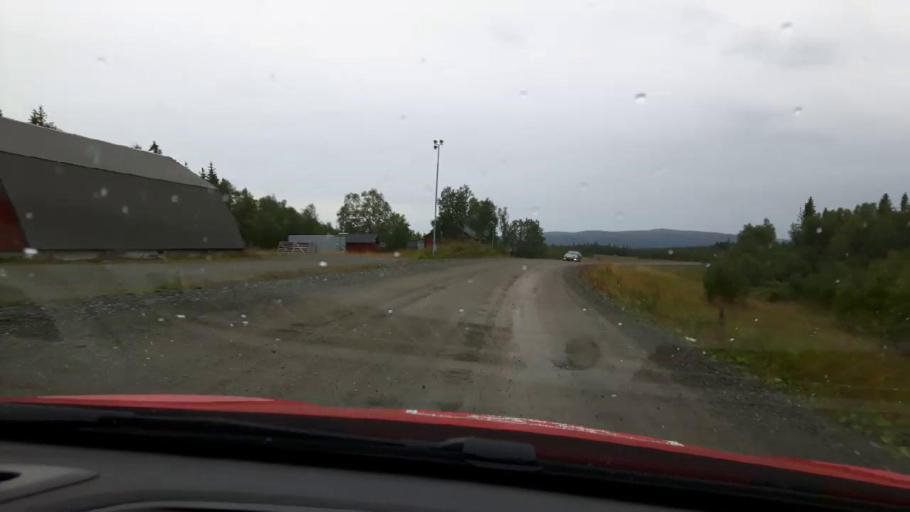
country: NO
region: Nord-Trondelag
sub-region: Meraker
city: Meraker
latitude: 63.5686
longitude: 12.2860
